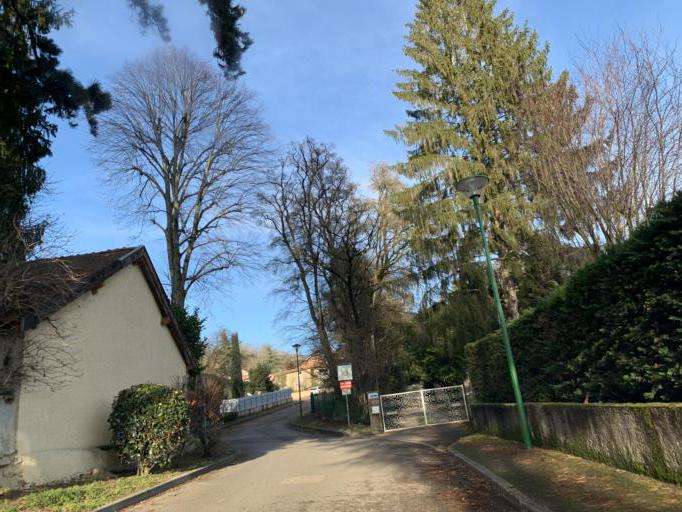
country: FR
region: Rhone-Alpes
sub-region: Departement de l'Ain
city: La Boisse
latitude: 45.8472
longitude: 5.0399
